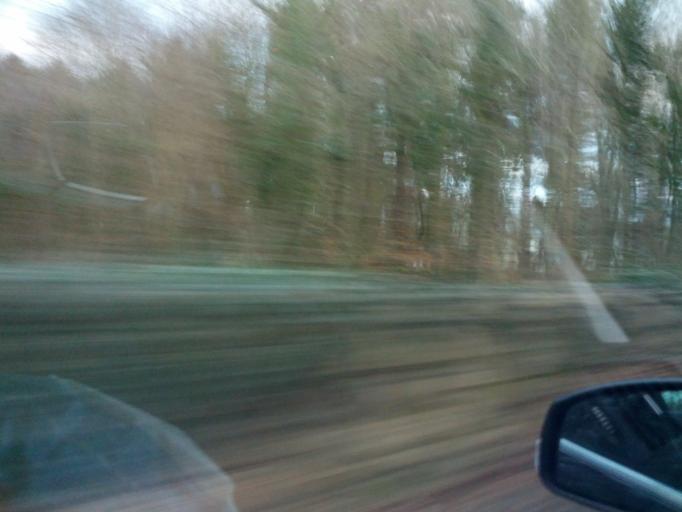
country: IE
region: Connaught
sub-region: County Galway
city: Athenry
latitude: 53.3367
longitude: -8.7717
